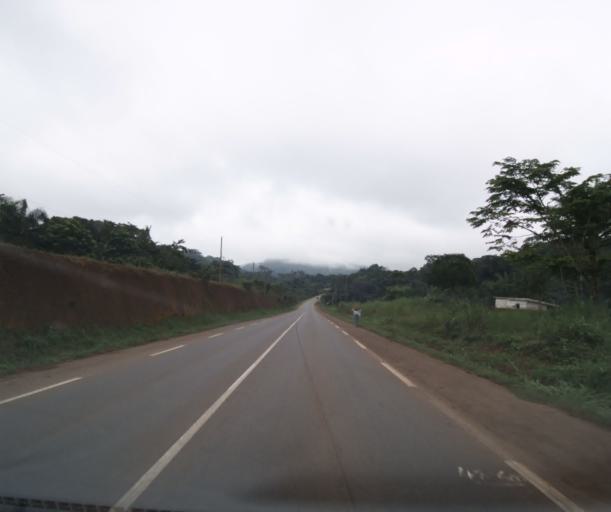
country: CM
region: Centre
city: Mbankomo
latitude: 3.7627
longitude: 11.1093
